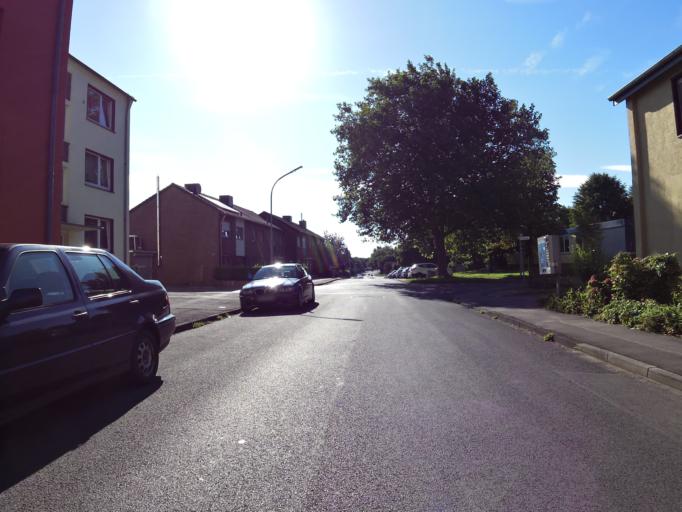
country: DE
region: North Rhine-Westphalia
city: Siersdorf
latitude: 50.8643
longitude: 6.2044
